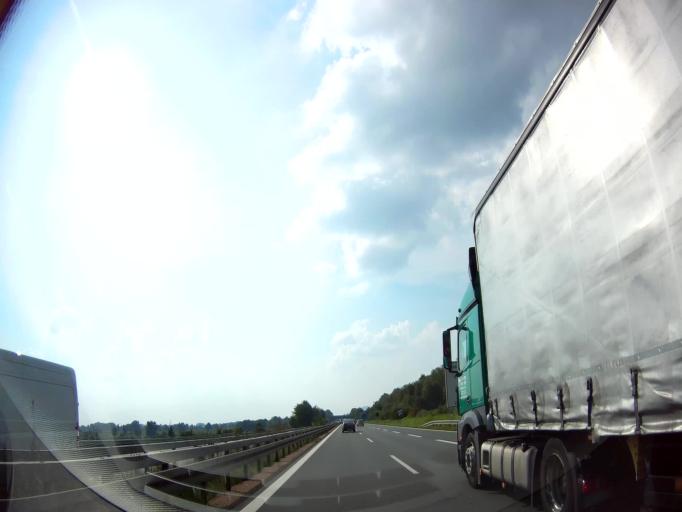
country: DE
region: Bavaria
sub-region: Upper Palatinate
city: Worth an der Donau
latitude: 48.9935
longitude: 12.4211
